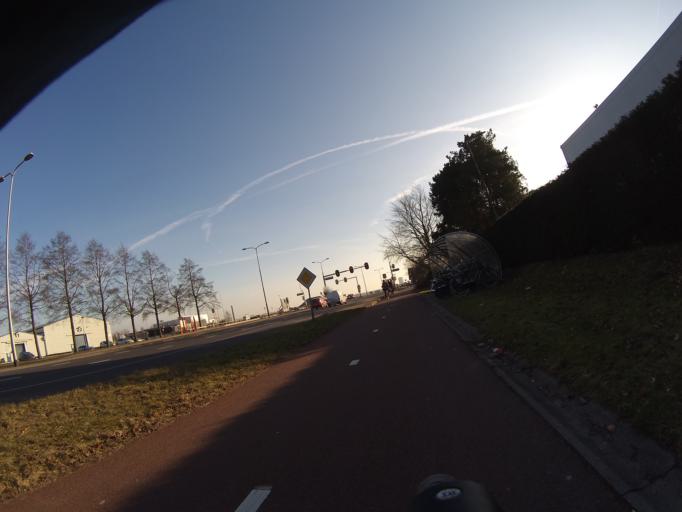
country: NL
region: Utrecht
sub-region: Gemeente Bunschoten
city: Bunschoten
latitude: 52.2279
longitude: 5.3701
